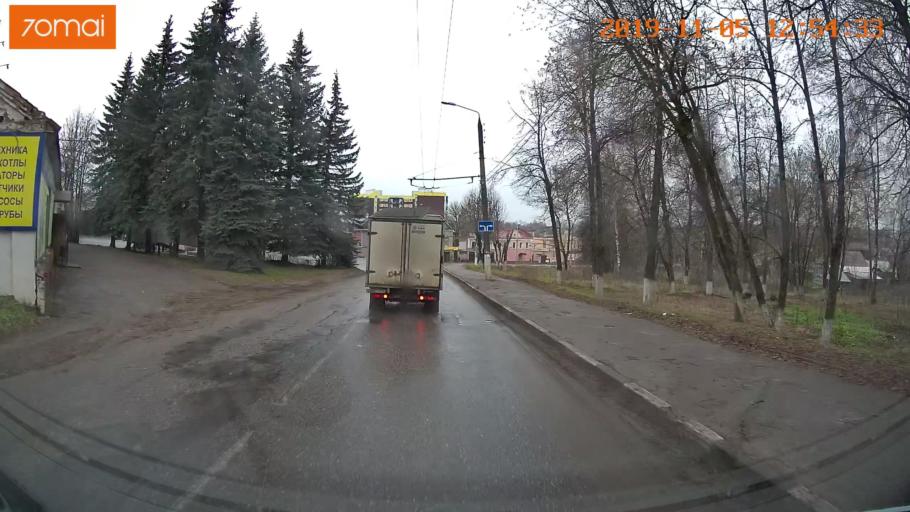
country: RU
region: Ivanovo
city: Kokhma
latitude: 56.9315
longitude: 41.0931
